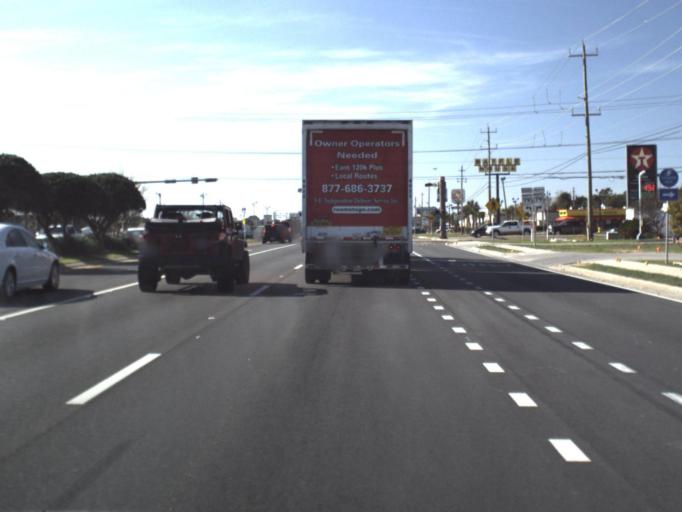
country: US
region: Florida
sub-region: Bay County
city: Laguna Beach
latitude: 30.2297
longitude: -85.8867
